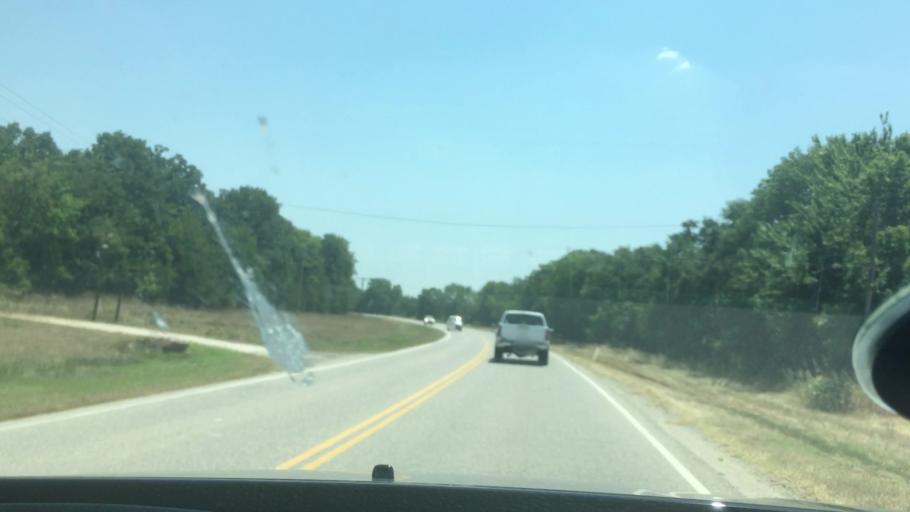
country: US
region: Oklahoma
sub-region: Bryan County
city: Durant
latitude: 34.1779
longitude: -96.4161
